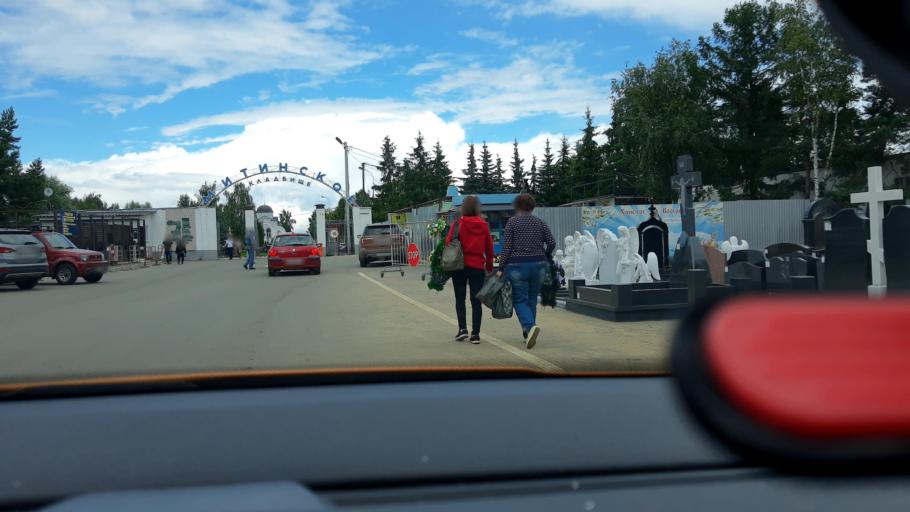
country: RU
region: Moskovskaya
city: Krasnogorsk
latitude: 55.8710
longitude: 37.3474
